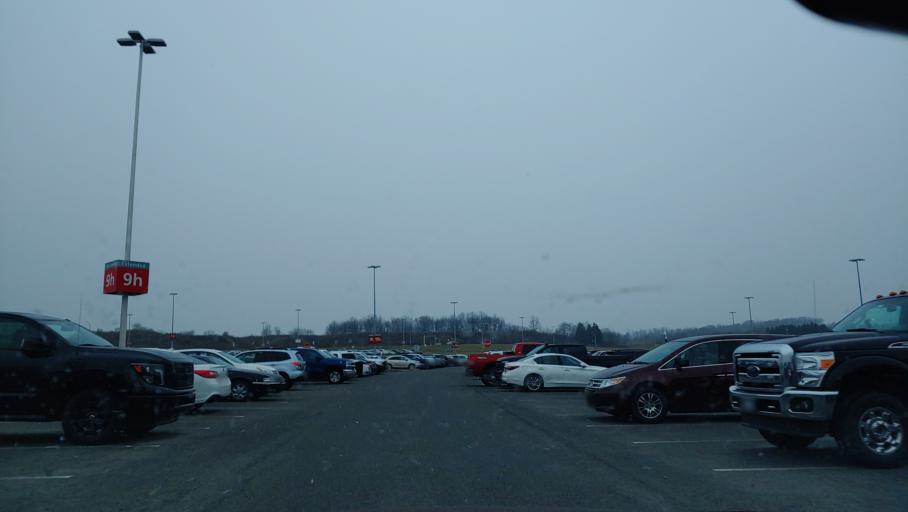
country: US
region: Pennsylvania
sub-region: Allegheny County
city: Imperial
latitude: 40.4920
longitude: -80.2621
